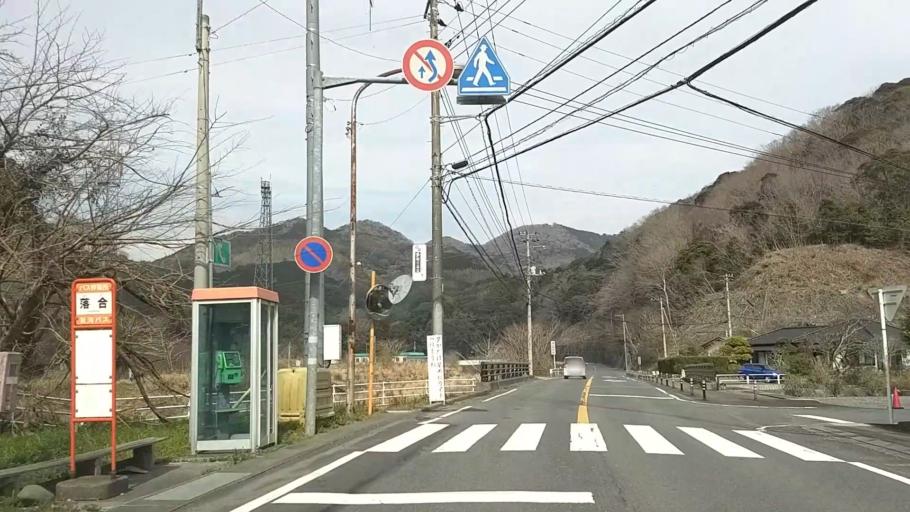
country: JP
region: Shizuoka
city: Shimoda
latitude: 34.7185
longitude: 138.9463
